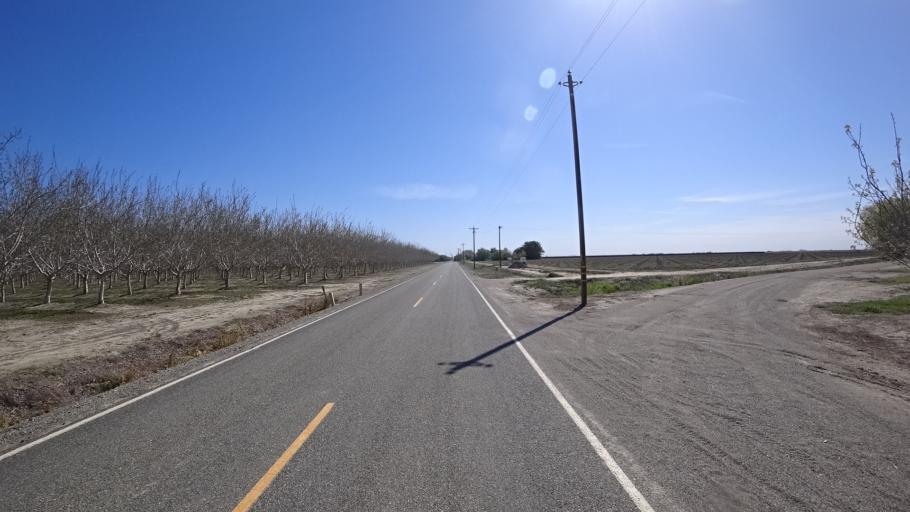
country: US
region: California
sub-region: Glenn County
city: Willows
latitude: 39.6235
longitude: -122.1084
